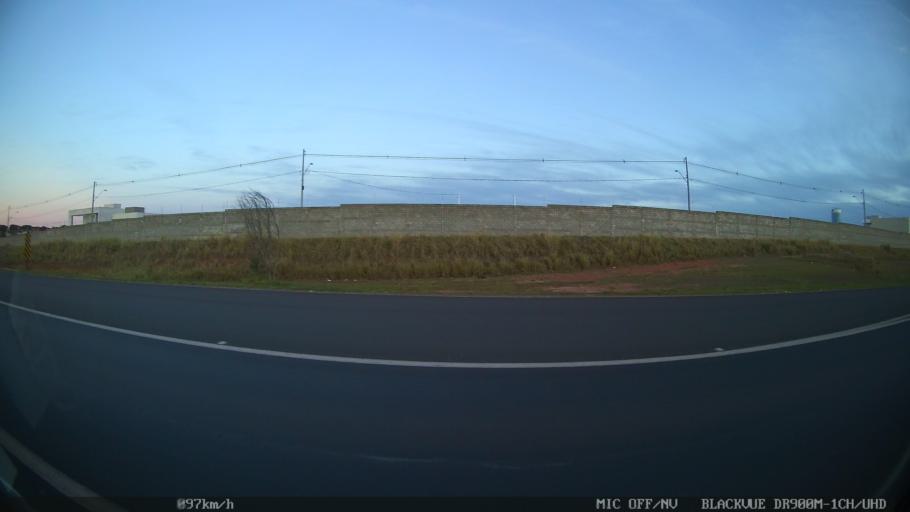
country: BR
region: Sao Paulo
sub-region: Catanduva
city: Catanduva
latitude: -21.1149
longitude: -48.9767
